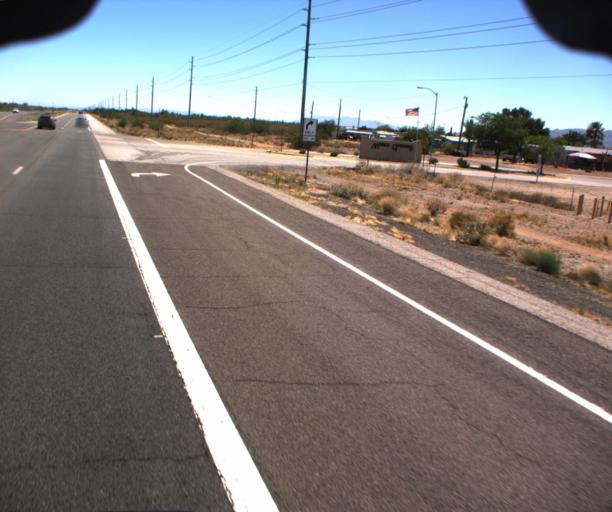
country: US
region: Arizona
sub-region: Maricopa County
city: Sun City West
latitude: 33.7890
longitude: -112.5431
